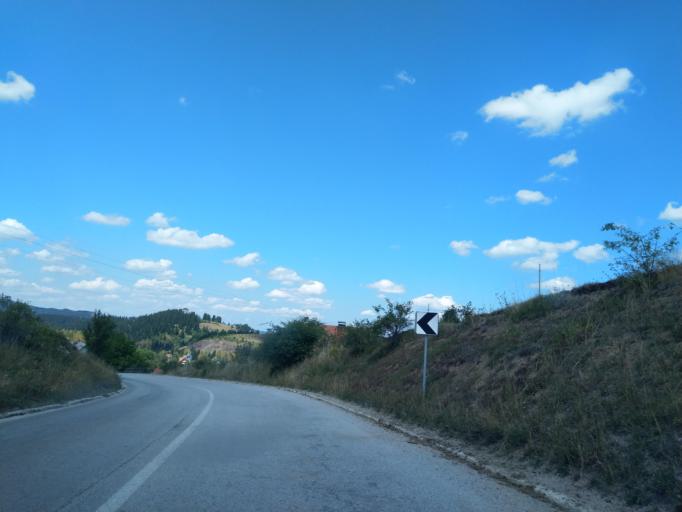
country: RS
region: Central Serbia
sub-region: Zlatiborski Okrug
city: Nova Varos
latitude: 43.4208
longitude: 19.8291
